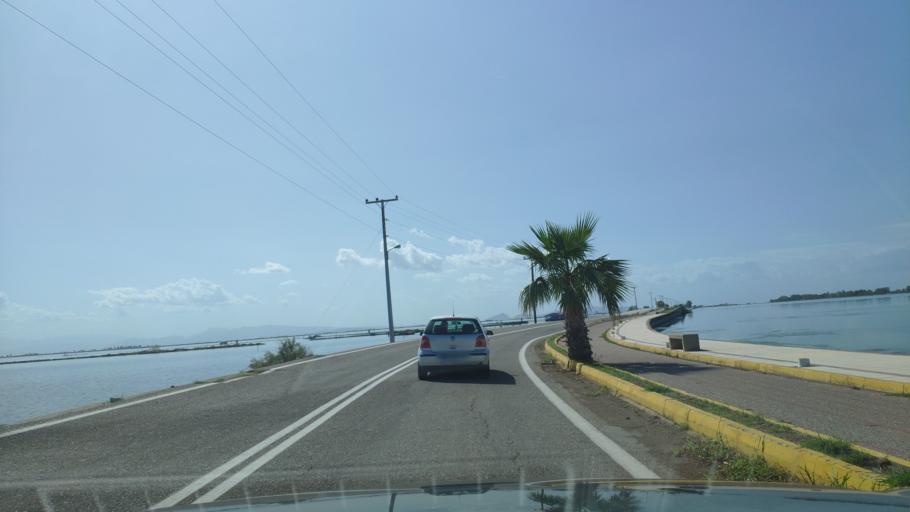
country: GR
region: West Greece
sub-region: Nomos Aitolias kai Akarnanias
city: Mesolongi
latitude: 38.3522
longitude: 21.4296
